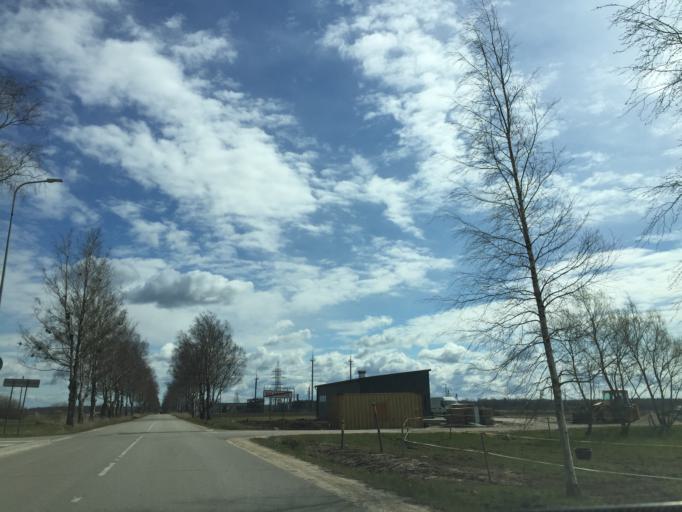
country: LV
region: Salacgrivas
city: Salacgriva
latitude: 57.7483
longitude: 24.3710
